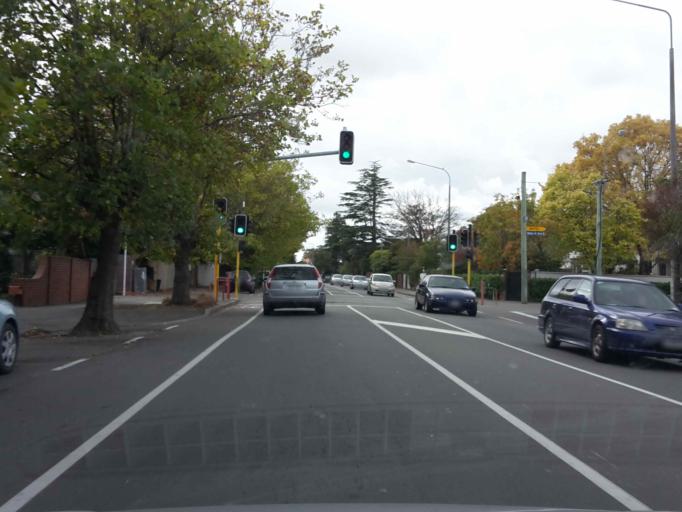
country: NZ
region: Canterbury
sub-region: Christchurch City
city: Christchurch
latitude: -43.5262
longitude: 172.6022
